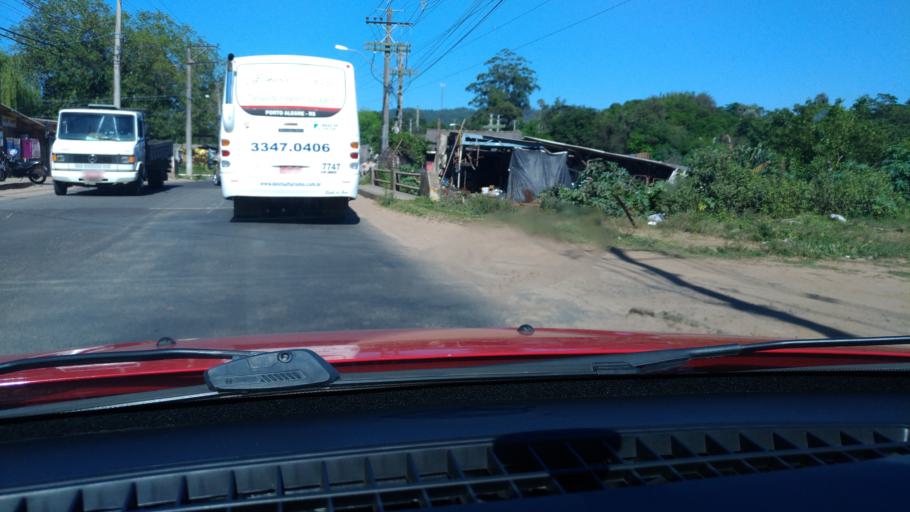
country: BR
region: Rio Grande do Sul
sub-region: Viamao
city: Viamao
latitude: -30.0461
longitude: -51.0847
